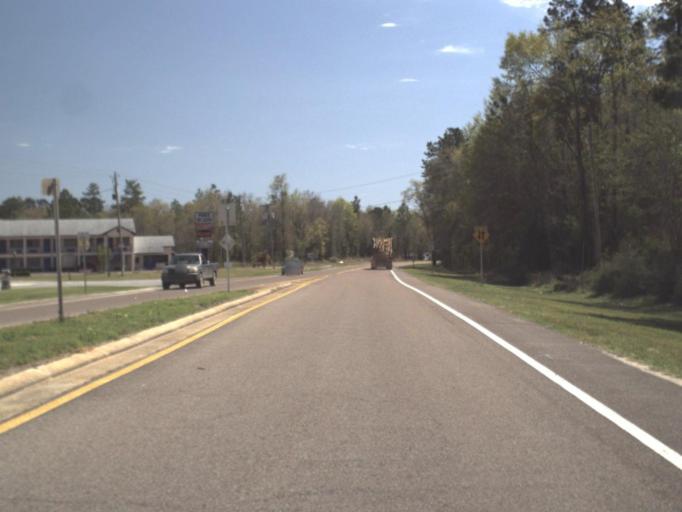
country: US
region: Florida
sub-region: Walton County
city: DeFuniak Springs
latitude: 30.7100
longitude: -85.9343
